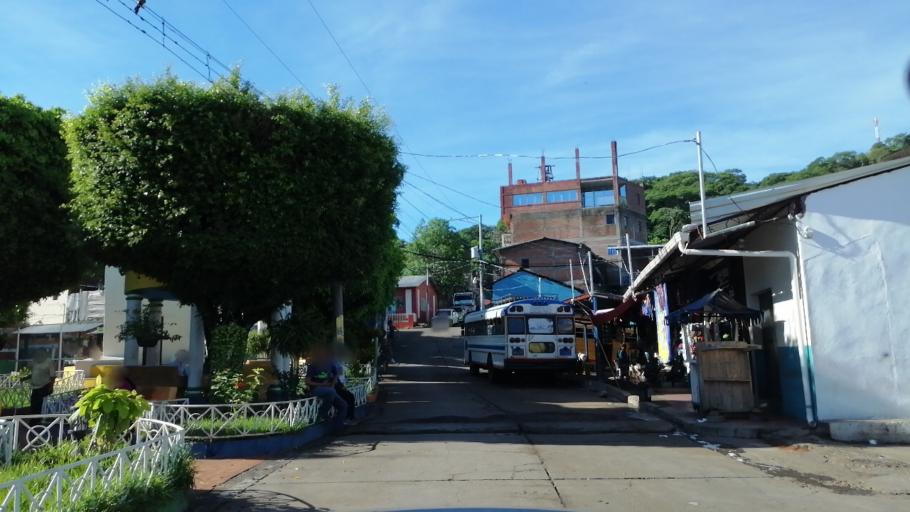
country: SV
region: Morazan
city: Cacaopera
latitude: 13.7736
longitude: -88.0796
